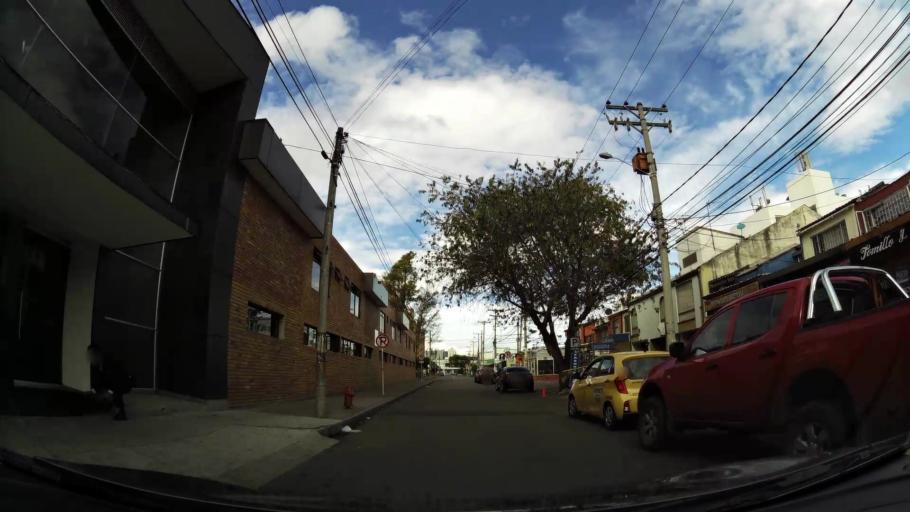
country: CO
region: Bogota D.C.
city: Barrio San Luis
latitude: 4.6985
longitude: -74.0733
